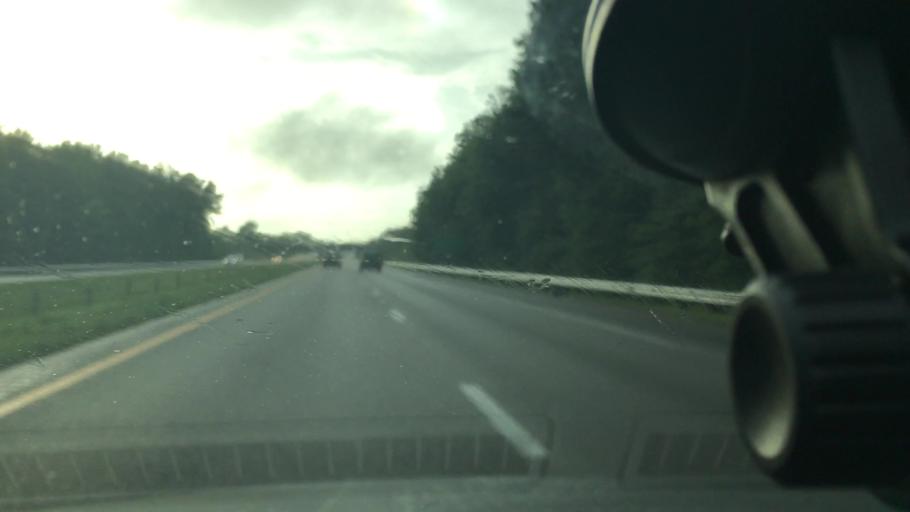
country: US
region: North Carolina
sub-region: Wilson County
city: Lucama
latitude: 35.7048
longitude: -77.9884
